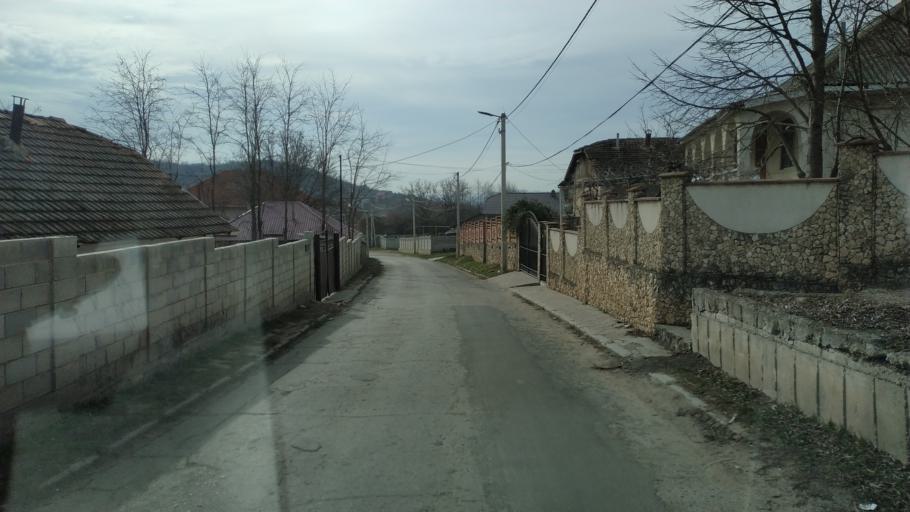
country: MD
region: Chisinau
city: Vatra
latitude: 47.0908
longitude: 28.7687
